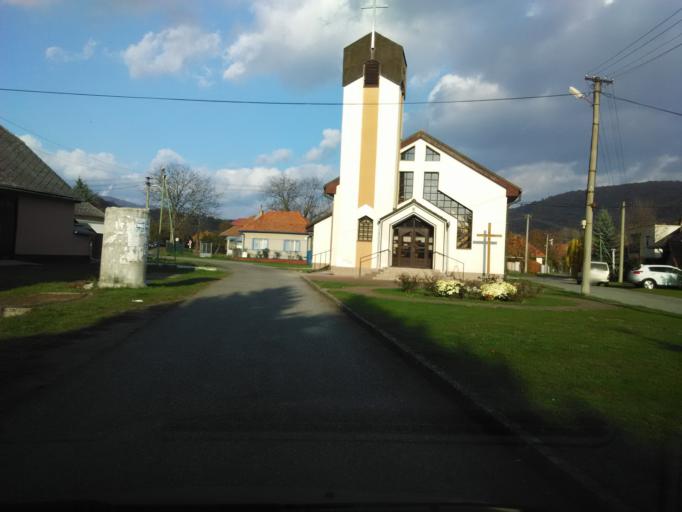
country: SK
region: Nitriansky
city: Tlmace
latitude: 48.3287
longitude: 18.5529
